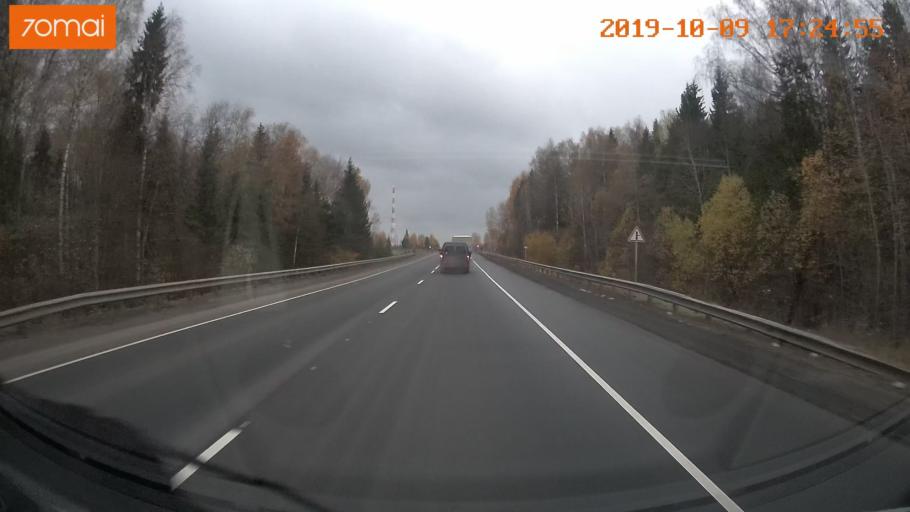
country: RU
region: Ivanovo
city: Furmanov
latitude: 57.1826
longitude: 41.0986
